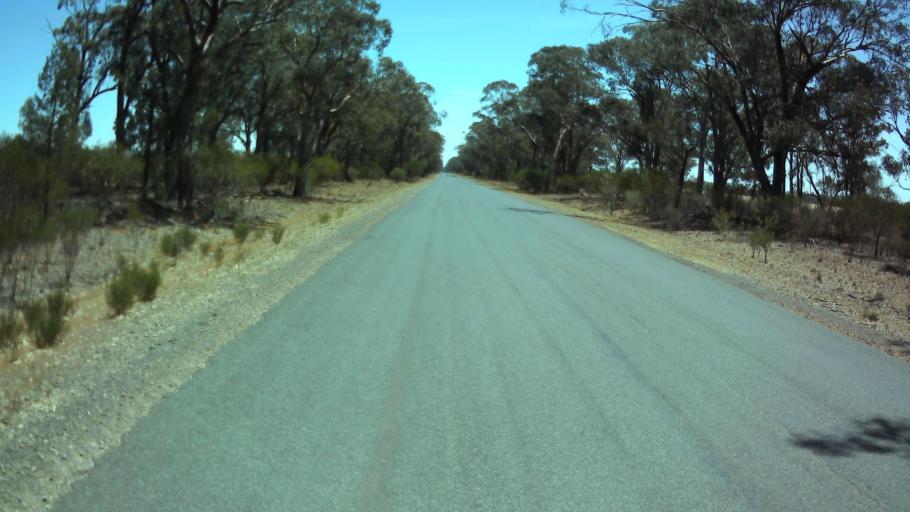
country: AU
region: New South Wales
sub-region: Weddin
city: Grenfell
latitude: -34.0204
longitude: 147.8506
